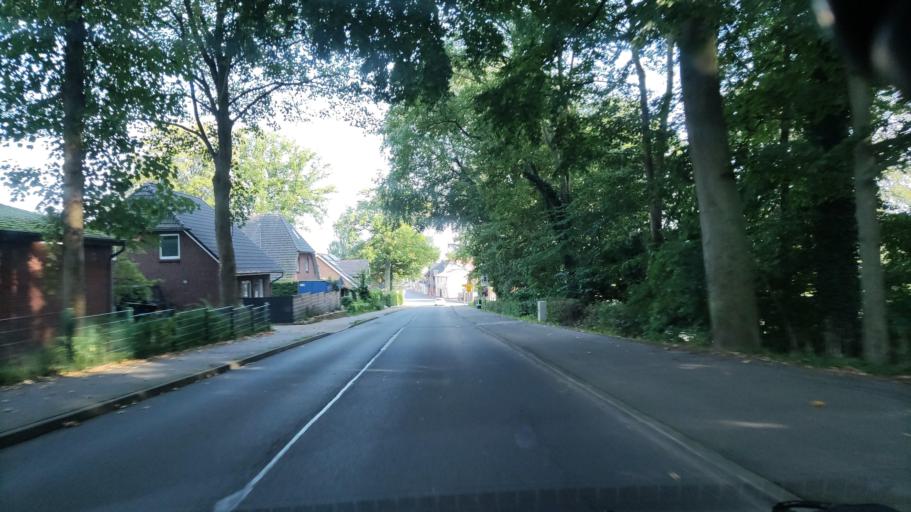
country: DE
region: Schleswig-Holstein
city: Bad Bramstedt
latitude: 53.9242
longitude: 9.8730
